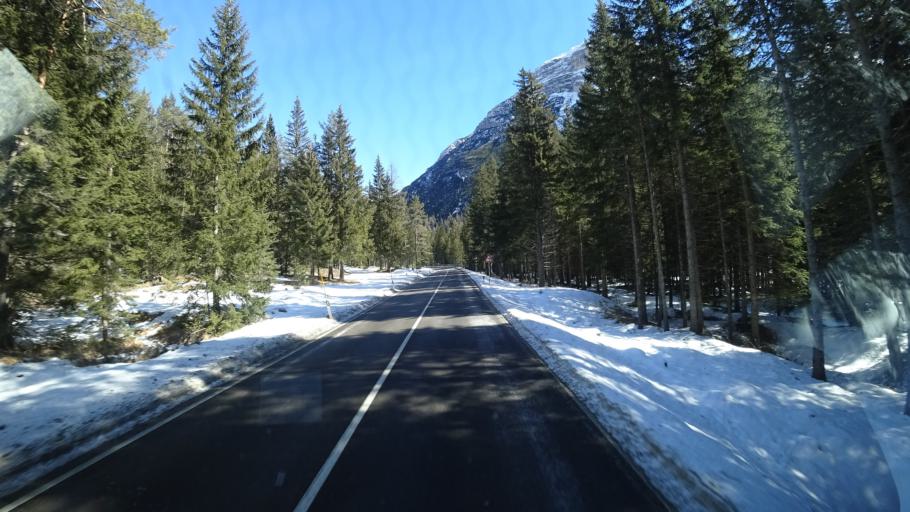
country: IT
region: Veneto
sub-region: Provincia di Belluno
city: Cortina d'Ampezzo
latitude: 46.6084
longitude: 12.1545
